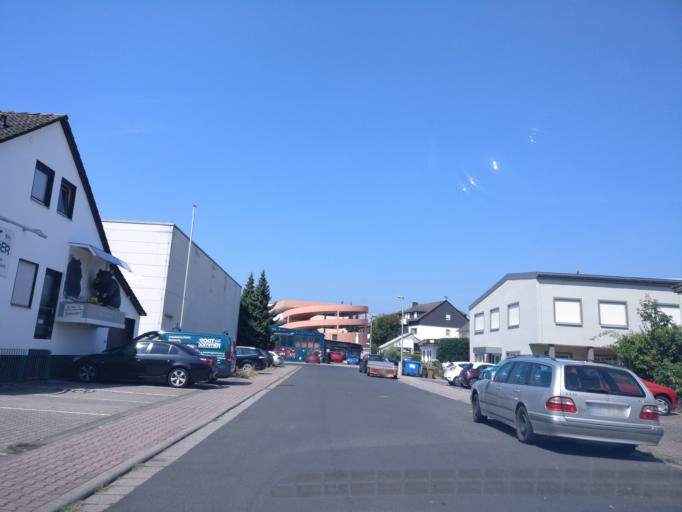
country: DE
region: Hesse
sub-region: Regierungsbezirk Darmstadt
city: Oberursel
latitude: 50.1877
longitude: 8.5882
